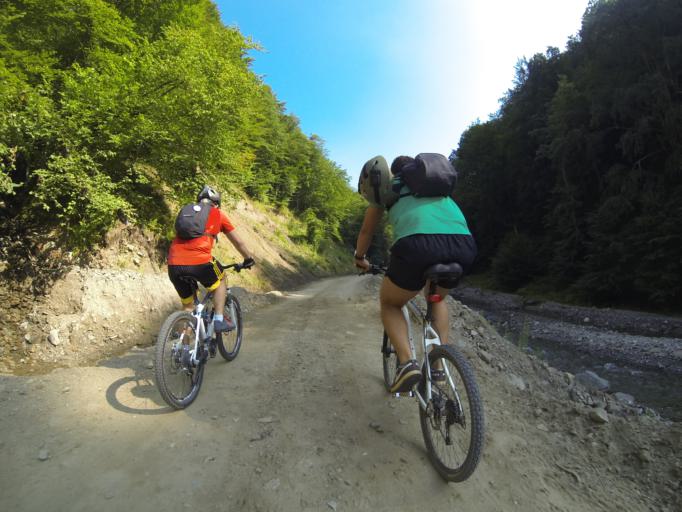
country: RO
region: Valcea
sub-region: Comuna Costesti
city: Bistrita
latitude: 45.2077
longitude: 23.9973
